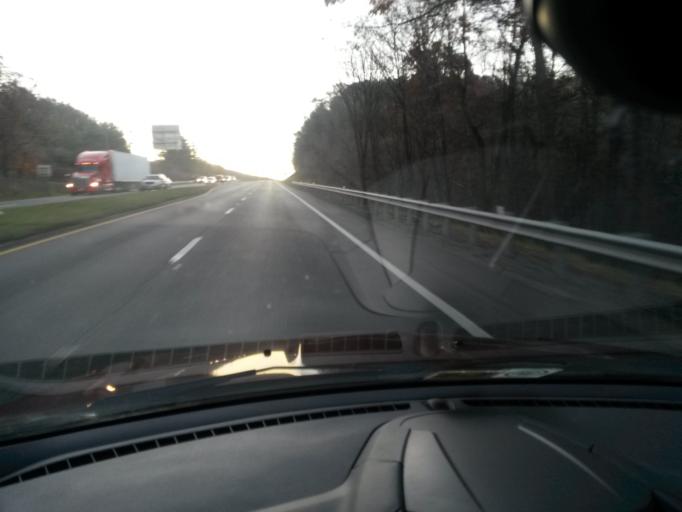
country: US
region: Virginia
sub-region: Roanoke County
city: Narrows
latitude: 37.2175
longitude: -79.9633
